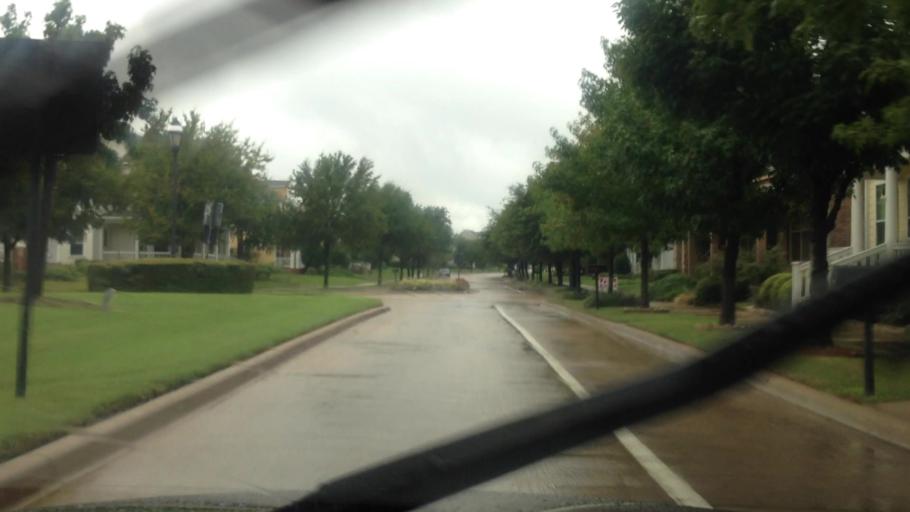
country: US
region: Texas
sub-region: Tarrant County
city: North Richland Hills
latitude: 32.8560
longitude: -97.2021
